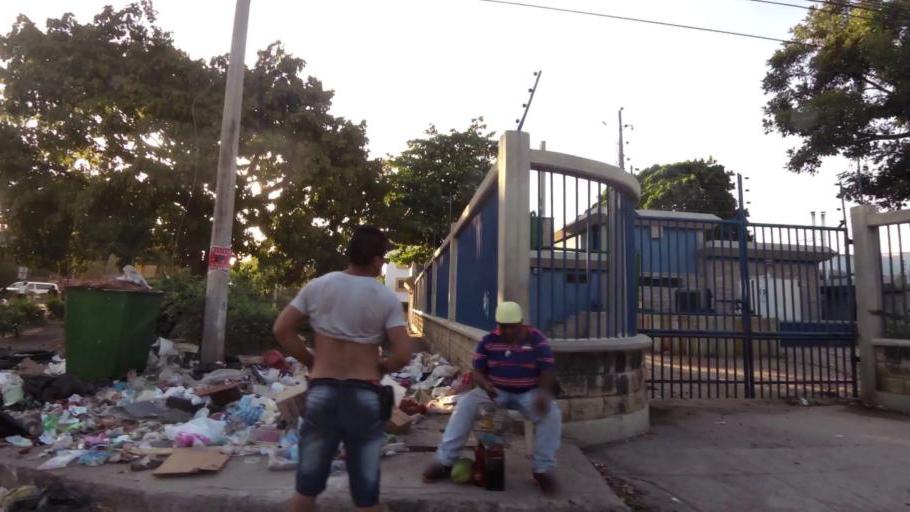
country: CO
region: Bolivar
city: Cartagena
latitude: 10.4057
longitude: -75.5214
